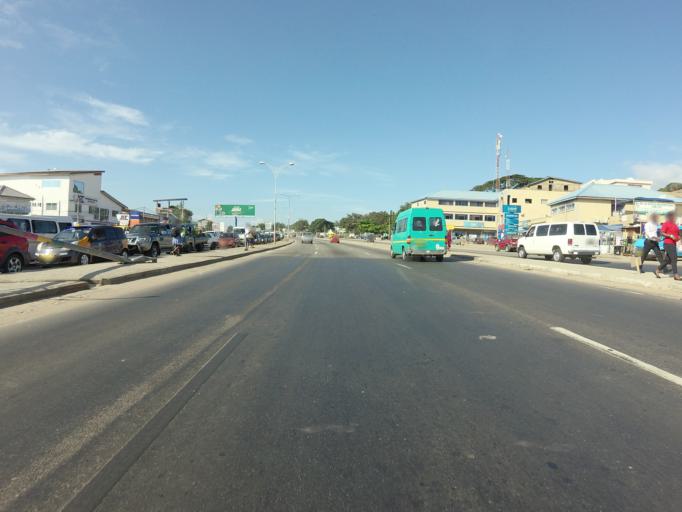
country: GH
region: Greater Accra
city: Gbawe
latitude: 5.5691
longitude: -0.2866
